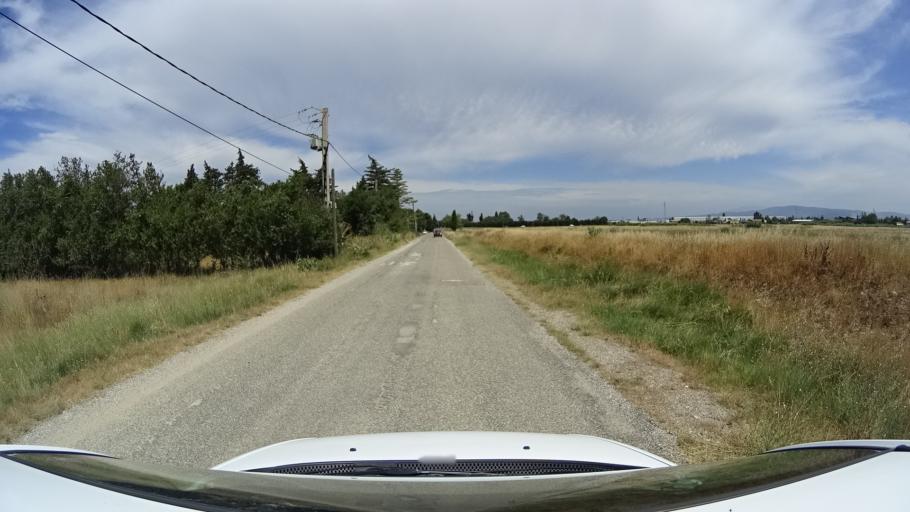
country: FR
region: Provence-Alpes-Cote d'Azur
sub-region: Departement du Vaucluse
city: Cheval-Blanc
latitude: 43.8203
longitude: 5.0563
